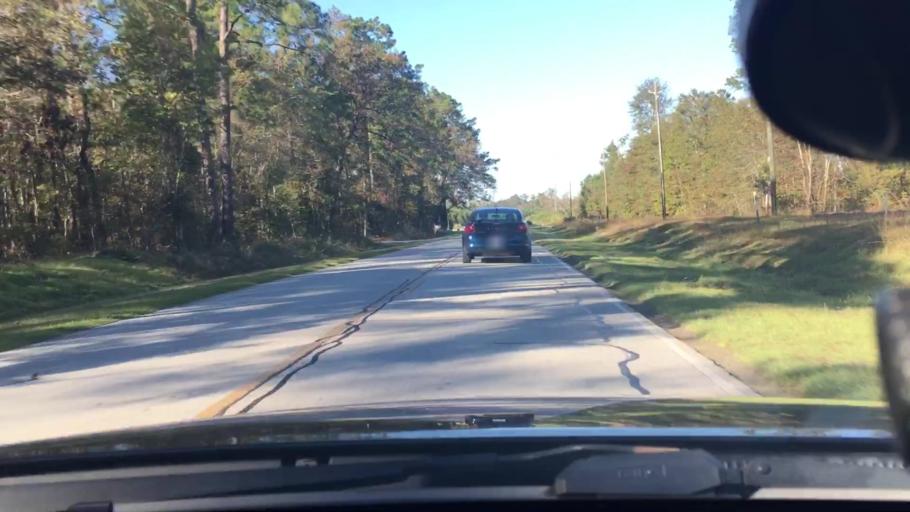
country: US
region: North Carolina
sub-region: Craven County
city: Vanceboro
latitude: 35.2775
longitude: -77.1531
